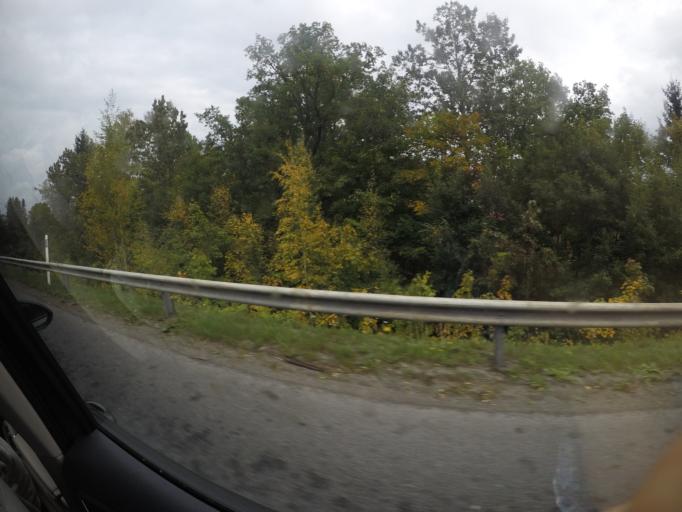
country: FI
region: Haeme
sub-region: Haemeenlinna
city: Parola
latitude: 61.0625
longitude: 24.3924
